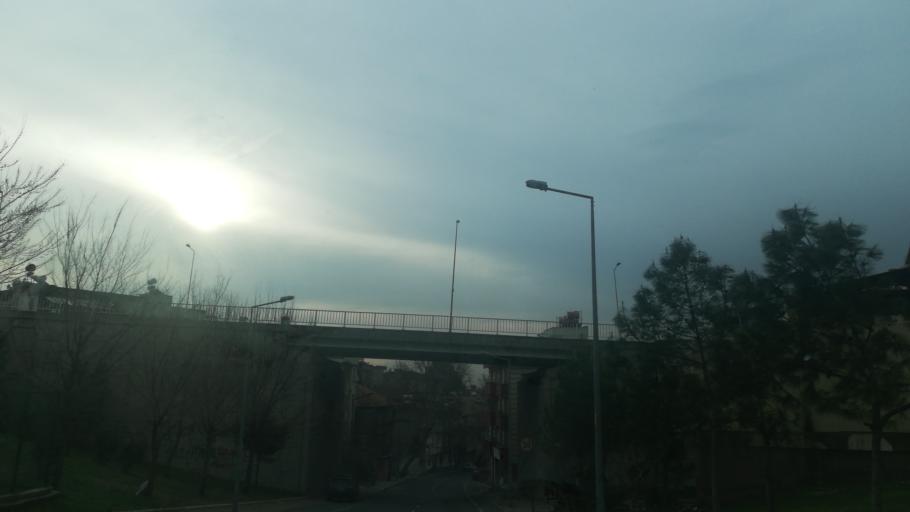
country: TR
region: Kahramanmaras
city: Kahramanmaras
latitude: 37.5927
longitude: 36.9262
